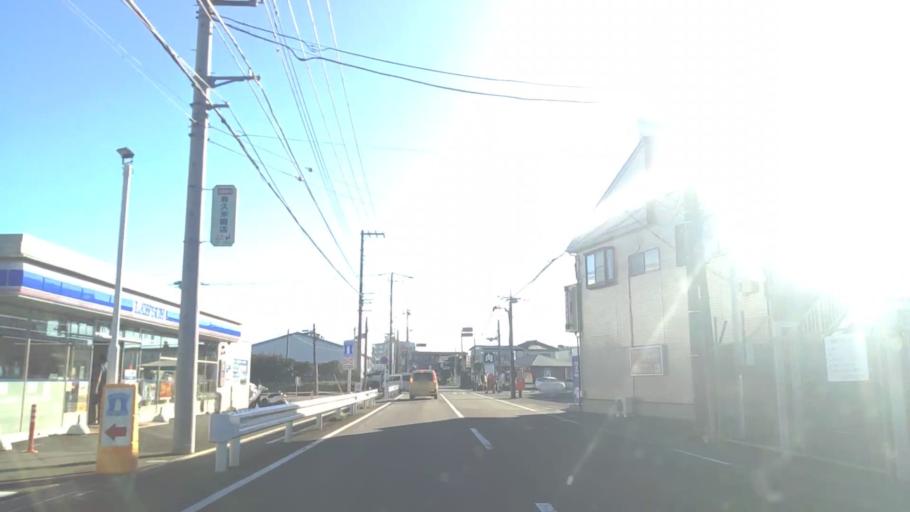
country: JP
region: Kanagawa
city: Atsugi
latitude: 35.3845
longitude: 139.3661
